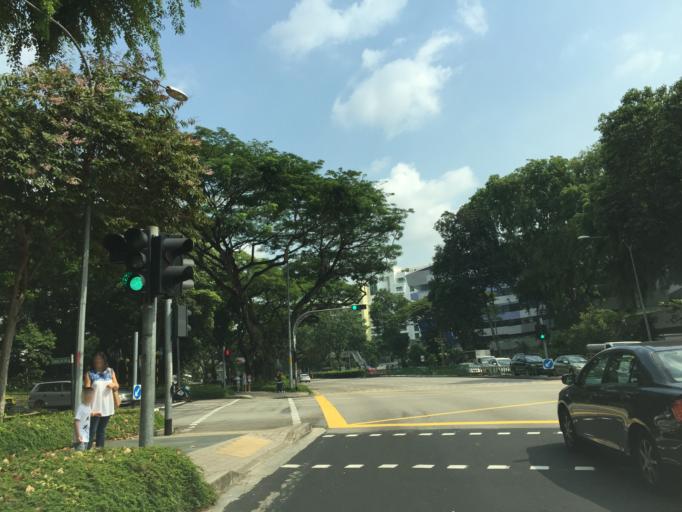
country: SG
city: Singapore
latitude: 1.3048
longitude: 103.8229
